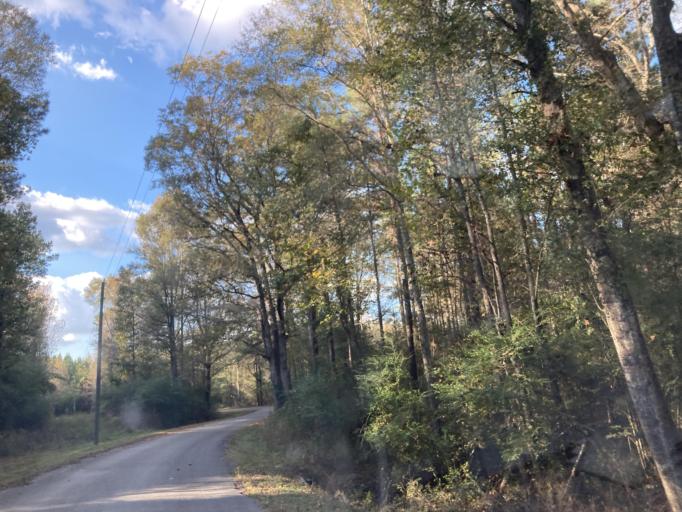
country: US
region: Mississippi
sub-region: Lamar County
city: Sumrall
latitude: 31.4458
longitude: -89.5862
